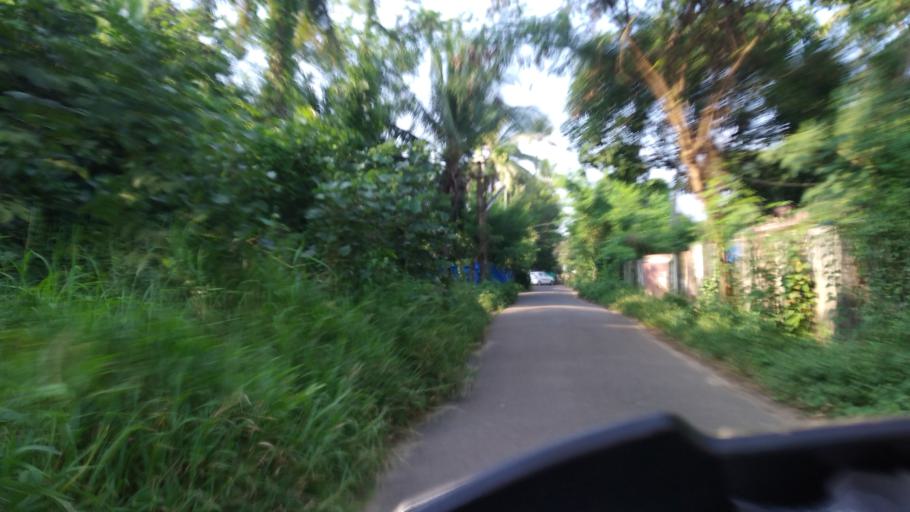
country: IN
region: Kerala
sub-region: Ernakulam
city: Elur
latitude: 10.0431
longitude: 76.2272
